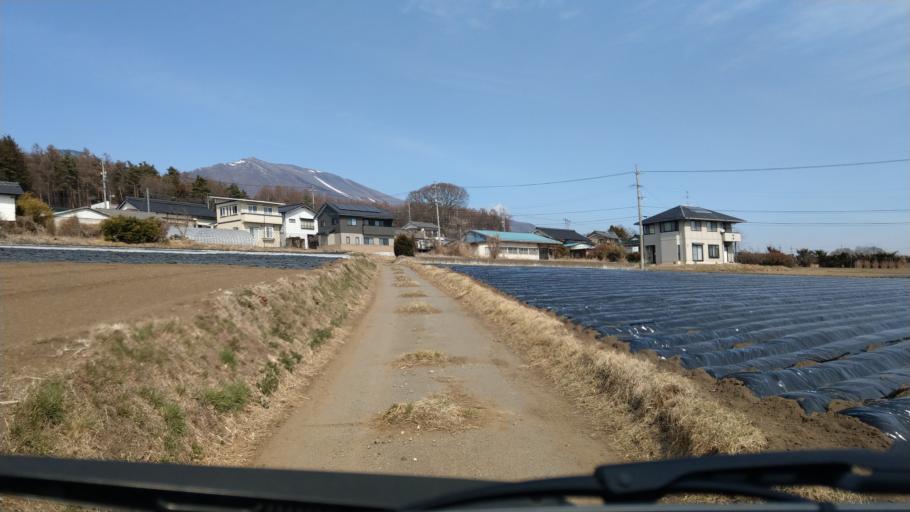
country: JP
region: Nagano
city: Komoro
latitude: 36.3330
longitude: 138.4623
